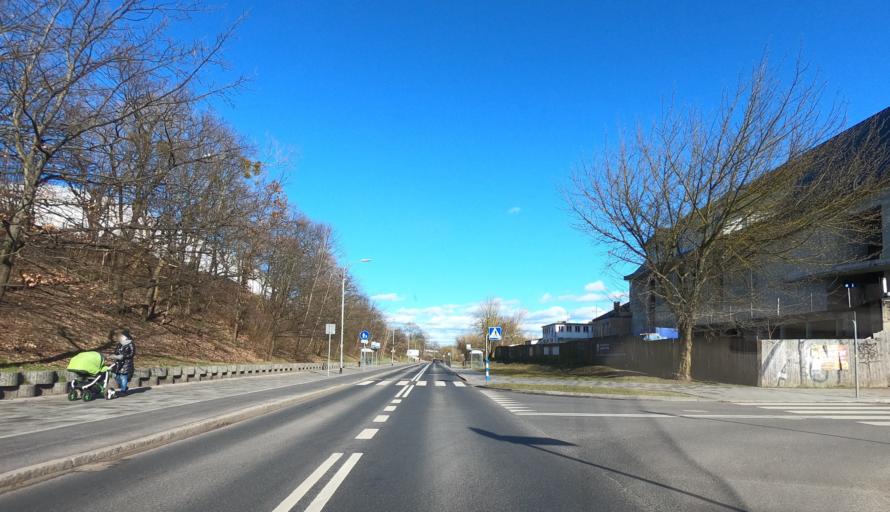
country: PL
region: West Pomeranian Voivodeship
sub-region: Szczecin
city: Szczecin
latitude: 53.4339
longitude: 14.5164
